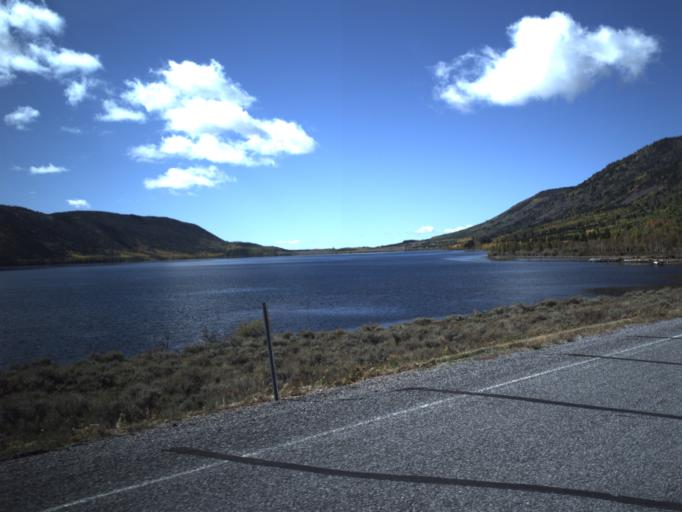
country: US
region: Utah
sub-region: Wayne County
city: Loa
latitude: 38.5632
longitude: -111.7027
